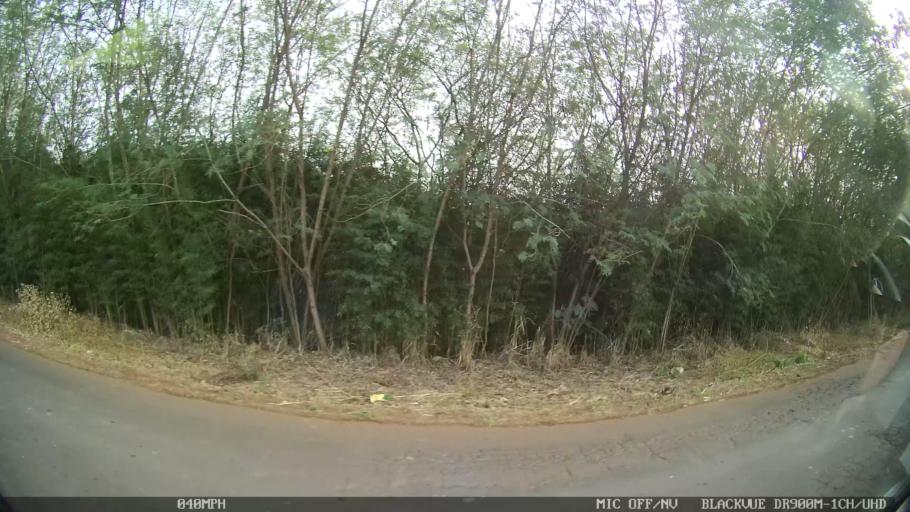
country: BR
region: Sao Paulo
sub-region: Piracicaba
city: Piracicaba
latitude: -22.7081
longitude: -47.5819
